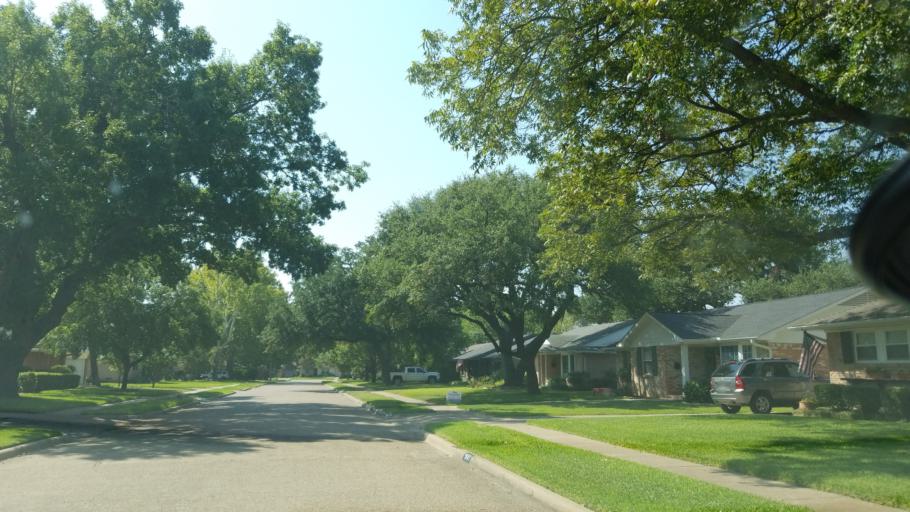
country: US
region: Texas
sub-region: Dallas County
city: Garland
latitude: 32.8784
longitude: -96.7026
